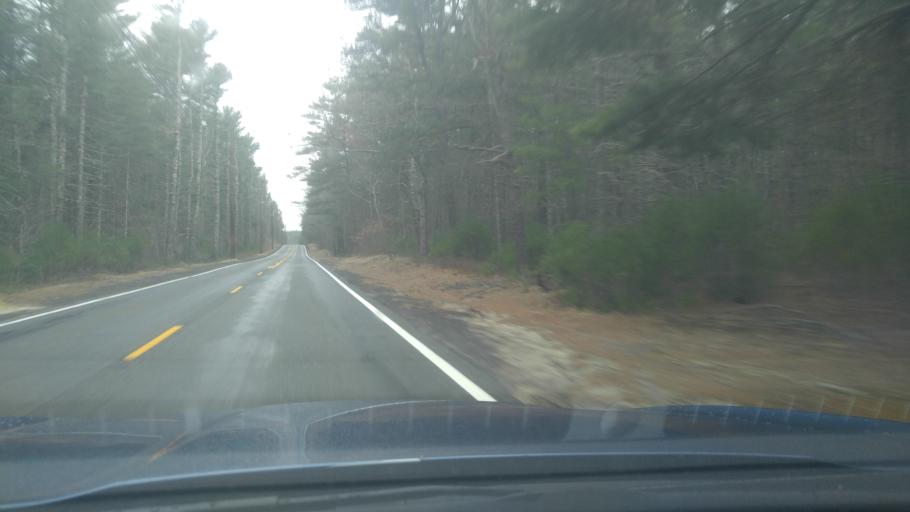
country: US
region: Rhode Island
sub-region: Kent County
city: West Greenwich
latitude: 41.6478
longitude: -71.5953
